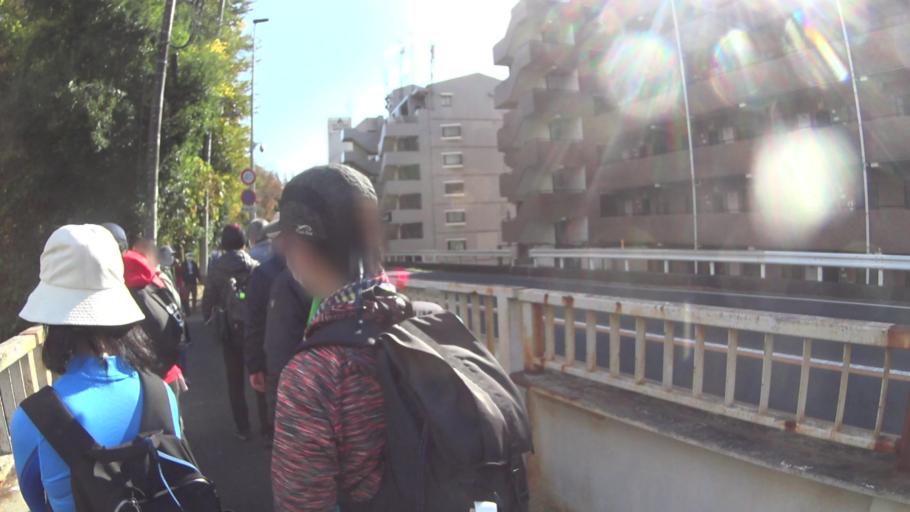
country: JP
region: Ibaraki
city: Mito-shi
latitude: 36.3719
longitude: 140.4820
